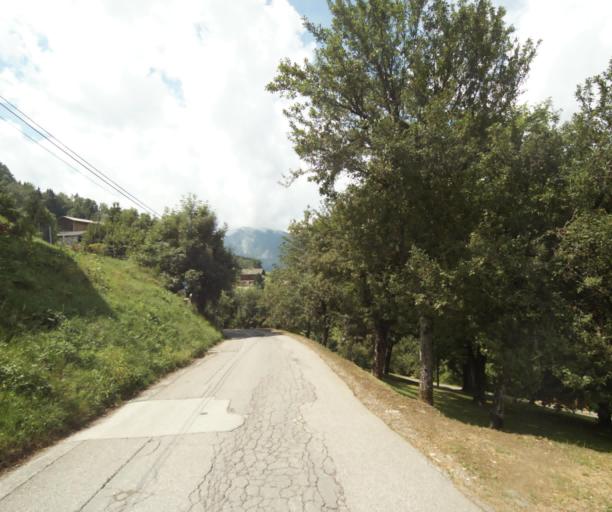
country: FR
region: Rhone-Alpes
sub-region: Departement de la Haute-Savoie
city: Thones
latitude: 45.8945
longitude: 6.3575
